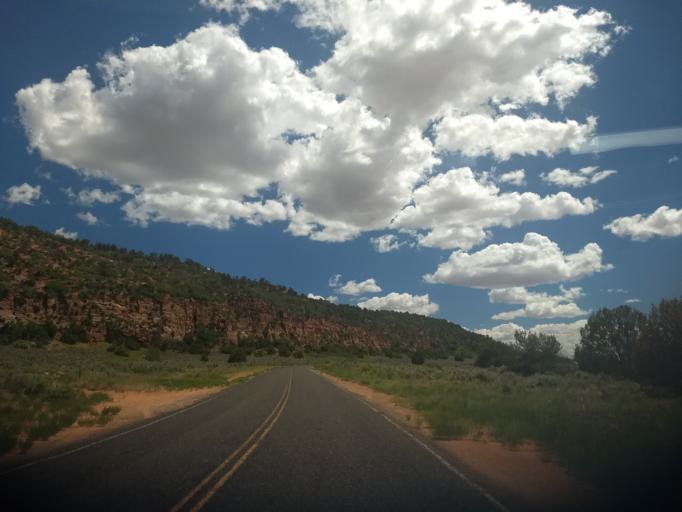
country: US
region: Utah
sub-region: Kane County
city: Kanab
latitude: 37.1054
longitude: -112.6812
